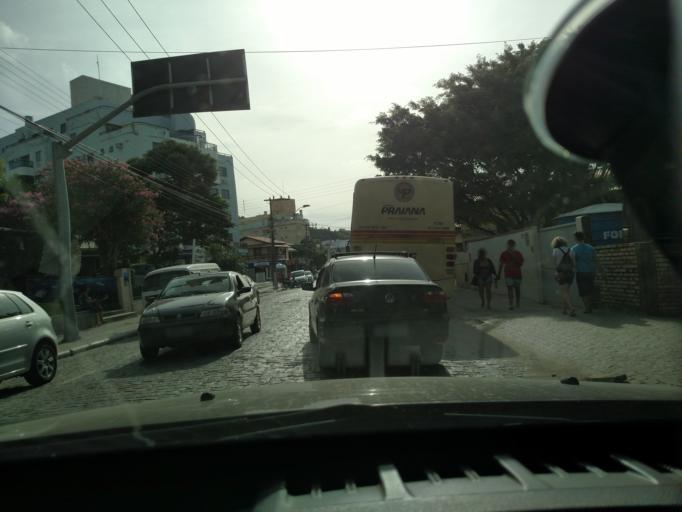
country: BR
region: Santa Catarina
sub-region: Porto Belo
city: Porto Belo
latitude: -27.1494
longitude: -48.4857
